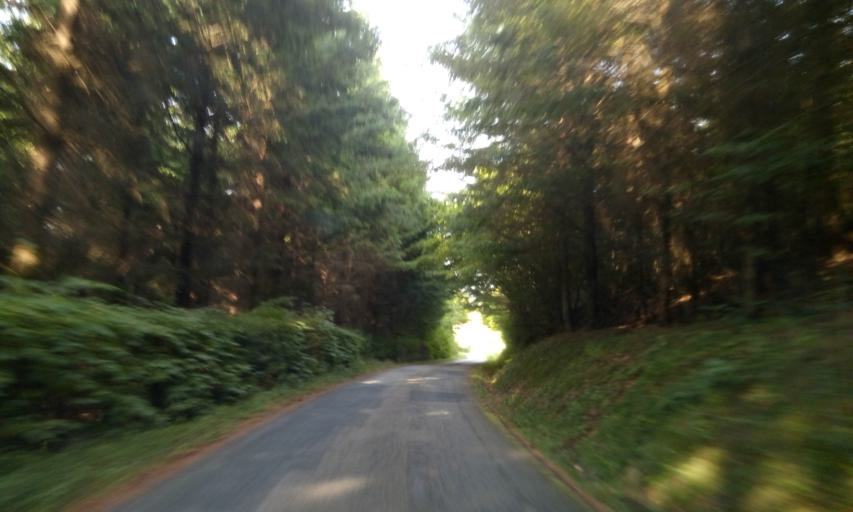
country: FR
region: Rhone-Alpes
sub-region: Departement du Rhone
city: Grandris
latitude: 45.9891
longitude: 4.4506
